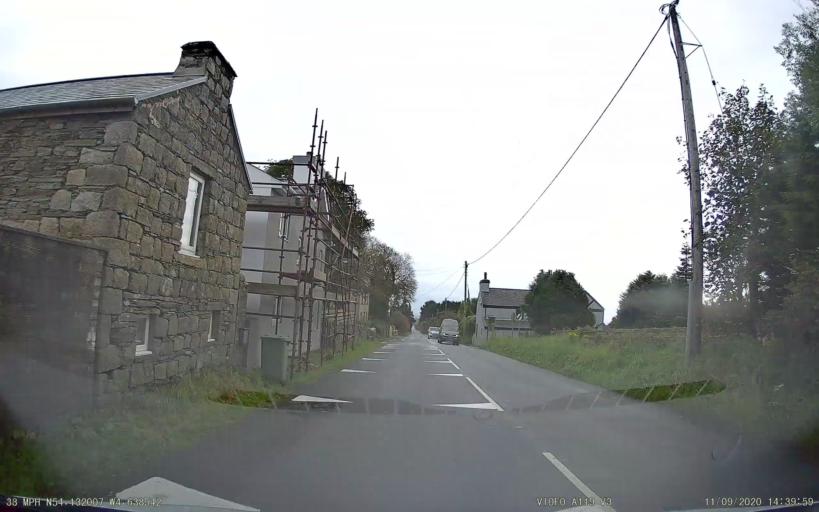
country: IM
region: Castletown
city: Castletown
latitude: 54.1320
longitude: -4.6385
